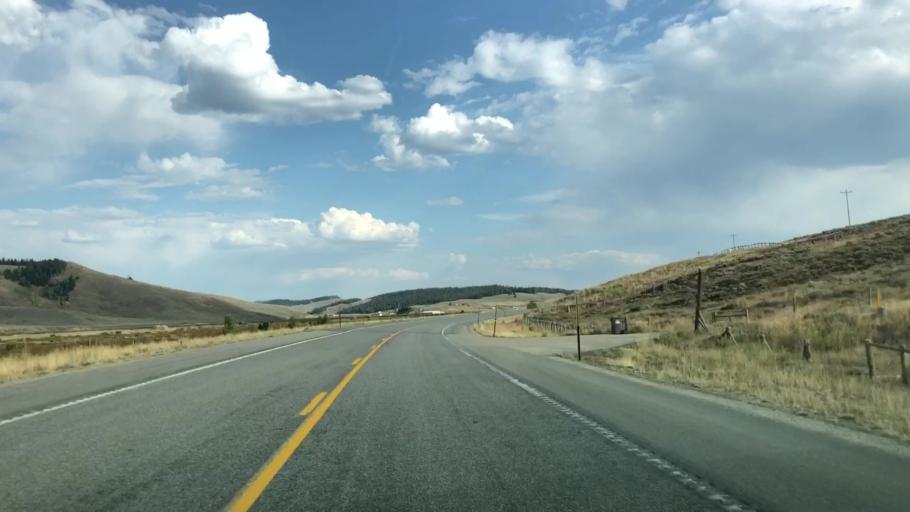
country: US
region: Wyoming
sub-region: Teton County
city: Hoback
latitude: 43.2242
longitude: -110.4301
